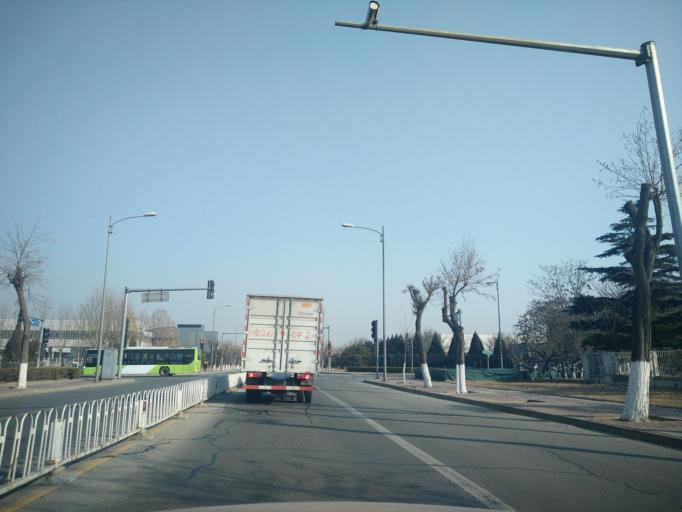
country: CN
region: Beijing
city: Jiugong
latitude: 39.7906
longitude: 116.5193
